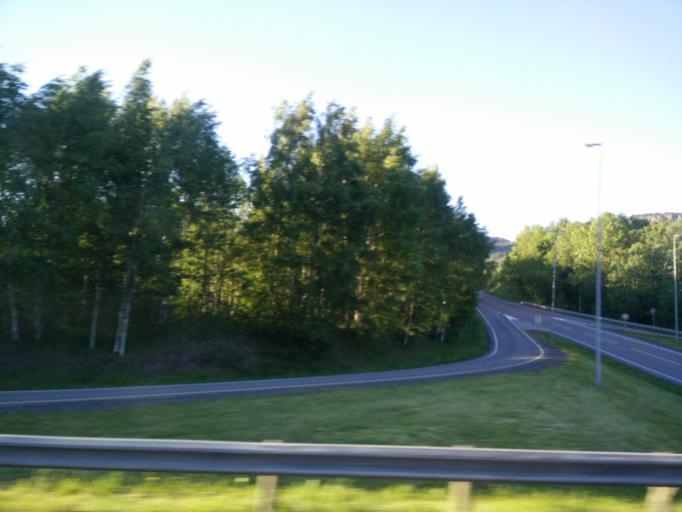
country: NO
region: Akershus
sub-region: Asker
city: Billingstad
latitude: 59.9074
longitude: 10.4852
